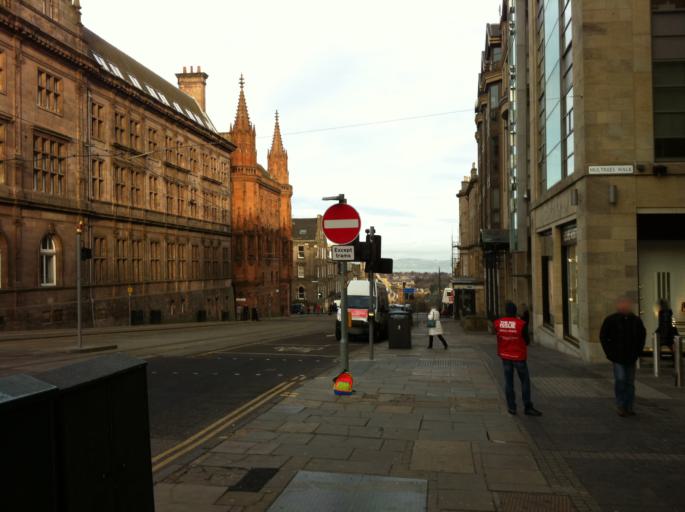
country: GB
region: Scotland
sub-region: Edinburgh
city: Edinburgh
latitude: 55.9549
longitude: -3.1923
